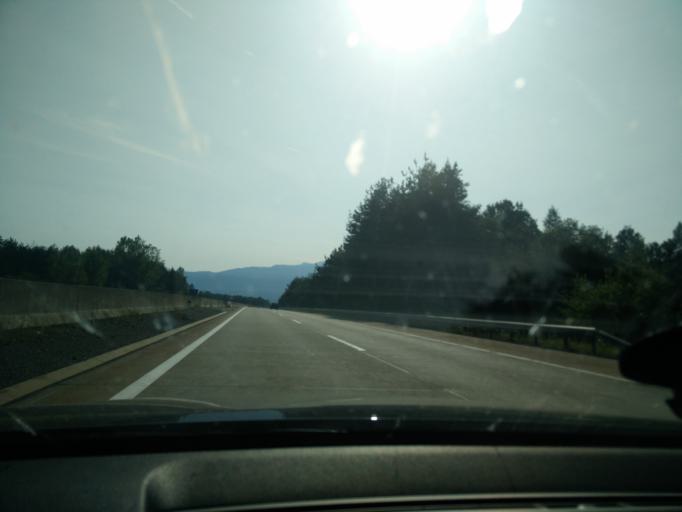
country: AT
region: Carinthia
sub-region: Politischer Bezirk Villach Land
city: Wernberg
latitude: 46.6228
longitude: 13.9494
